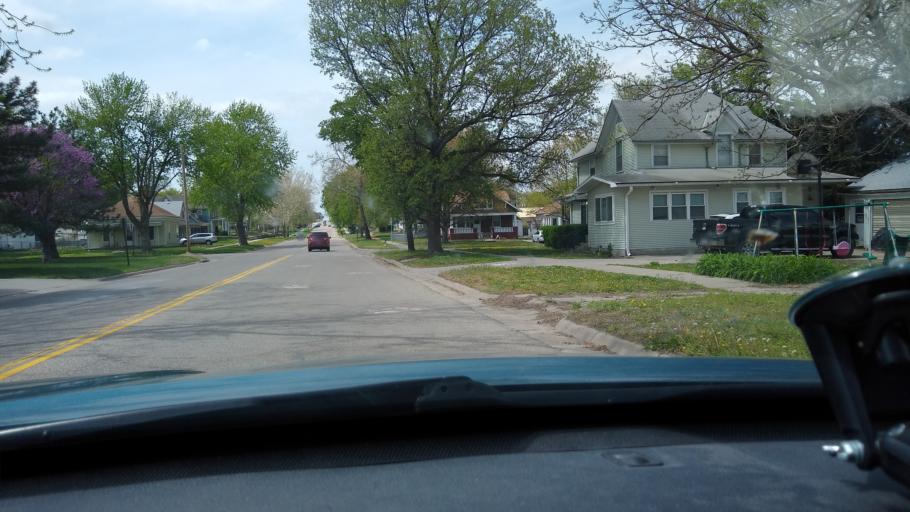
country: US
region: Kansas
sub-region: Cloud County
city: Concordia
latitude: 39.5665
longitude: -97.6584
